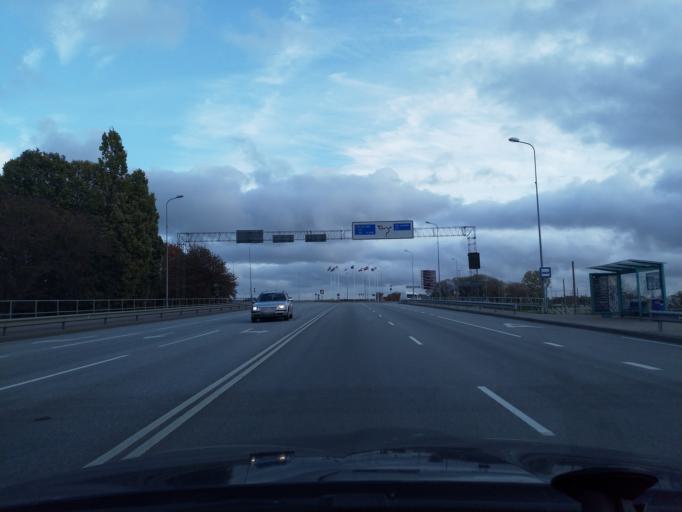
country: LV
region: Ventspils
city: Ventspils
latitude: 57.3876
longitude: 21.5835
